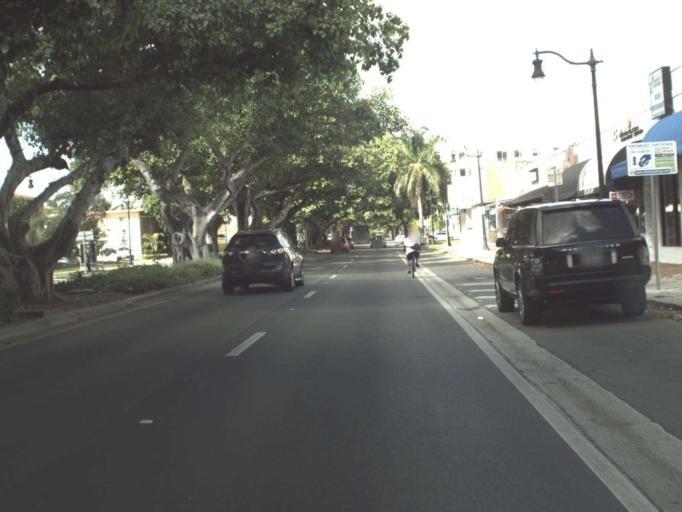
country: US
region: Florida
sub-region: Miami-Dade County
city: Coconut Grove
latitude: 25.7506
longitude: -80.2331
